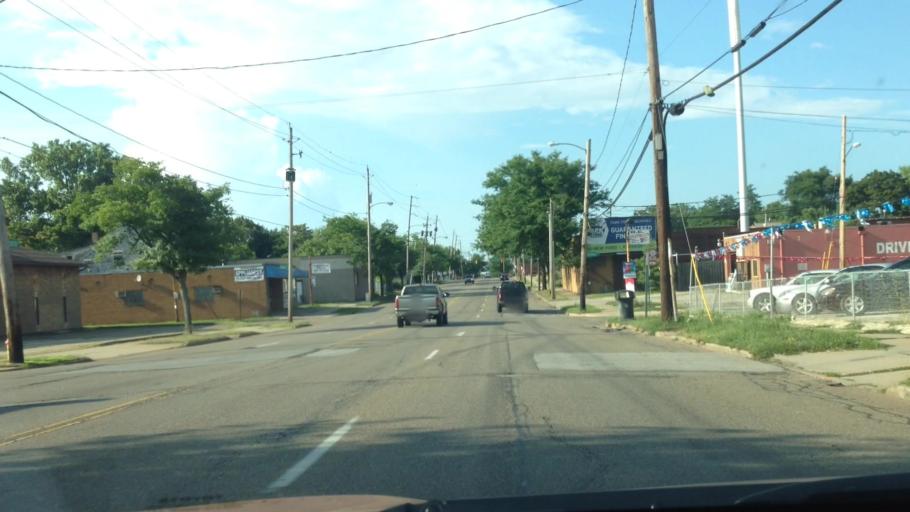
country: US
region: Ohio
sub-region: Summit County
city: Akron
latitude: 41.0514
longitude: -81.4910
